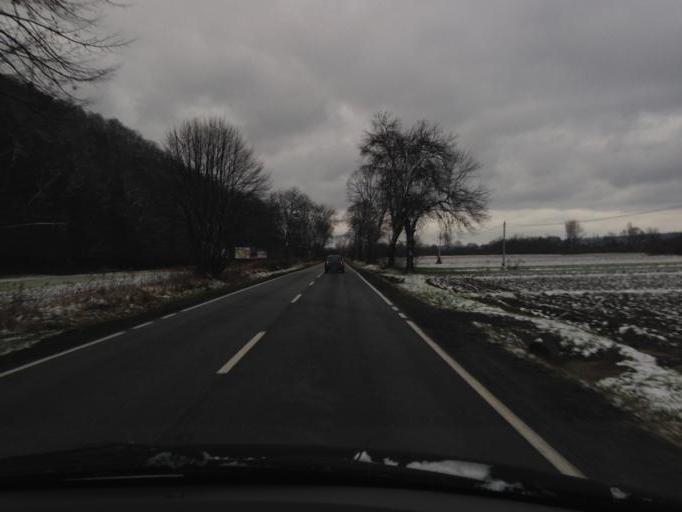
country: PL
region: Lesser Poland Voivodeship
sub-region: Powiat tarnowski
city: Zakliczyn
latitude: 49.8678
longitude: 20.7682
